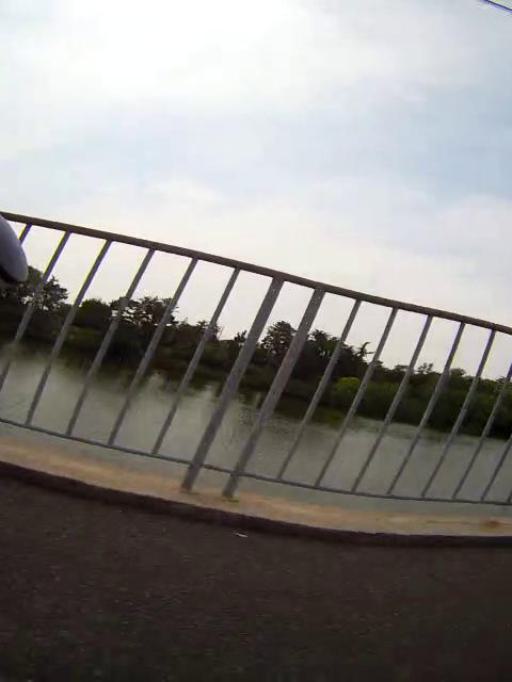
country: JP
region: Osaka
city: Toyonaka
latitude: 34.7729
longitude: 135.4906
